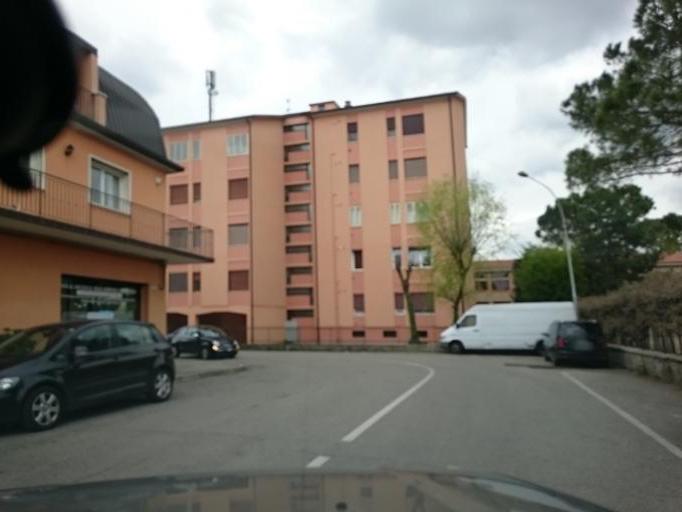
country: IT
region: Veneto
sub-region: Provincia di Padova
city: Padova
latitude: 45.3947
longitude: 11.9022
